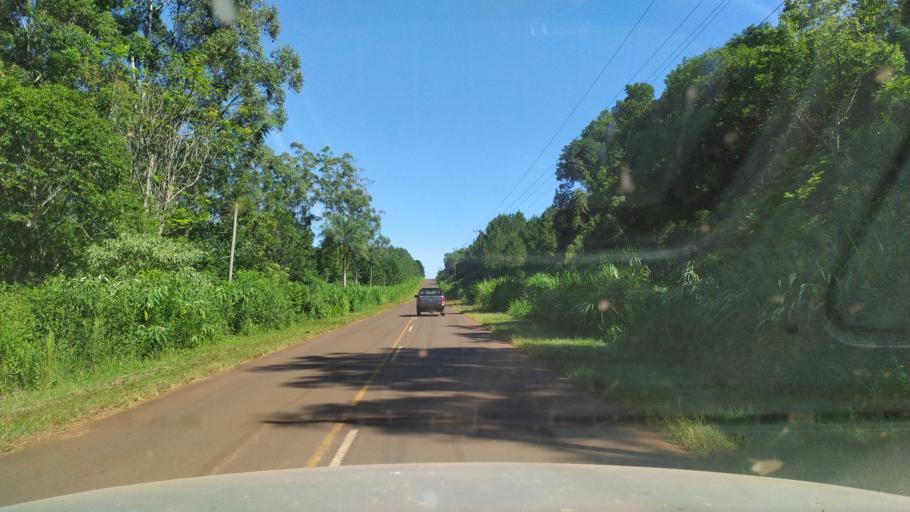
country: AR
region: Misiones
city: Caraguatay
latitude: -26.6787
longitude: -54.7183
